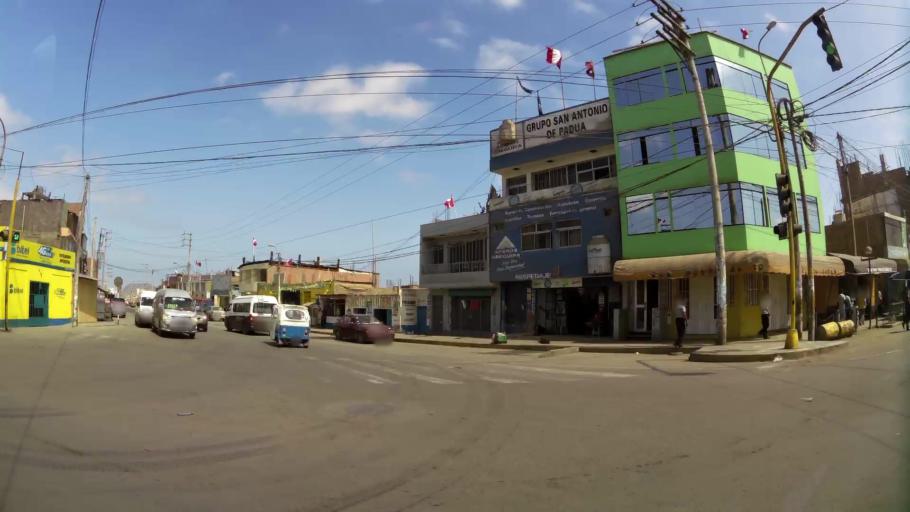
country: PE
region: Lima
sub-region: Provincia de Canete
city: Mala
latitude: -12.6562
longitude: -76.6363
